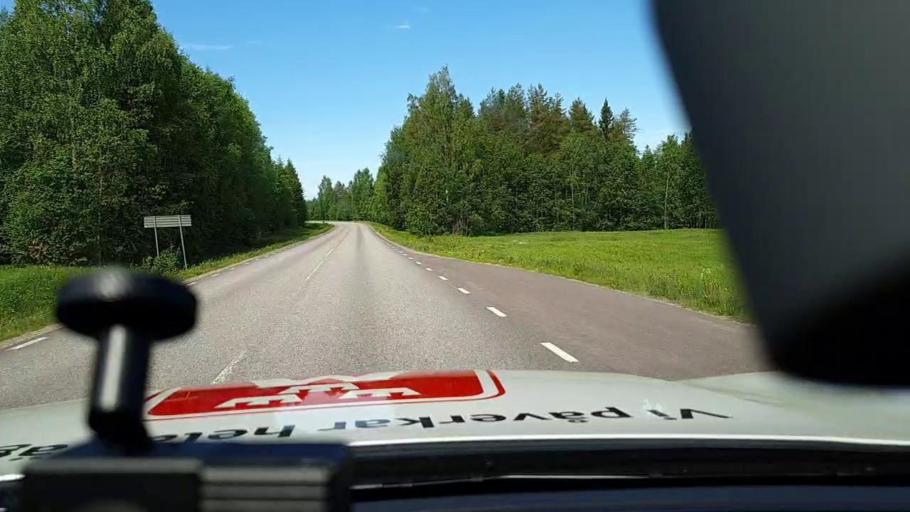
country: SE
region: Norrbotten
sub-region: Lulea Kommun
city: Sodra Sunderbyn
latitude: 65.6580
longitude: 21.8422
